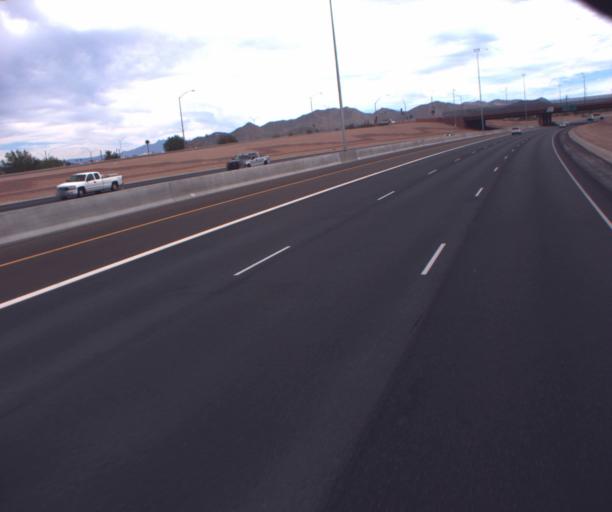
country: US
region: Arizona
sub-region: Maricopa County
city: Mesa
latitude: 33.4816
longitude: -111.7219
